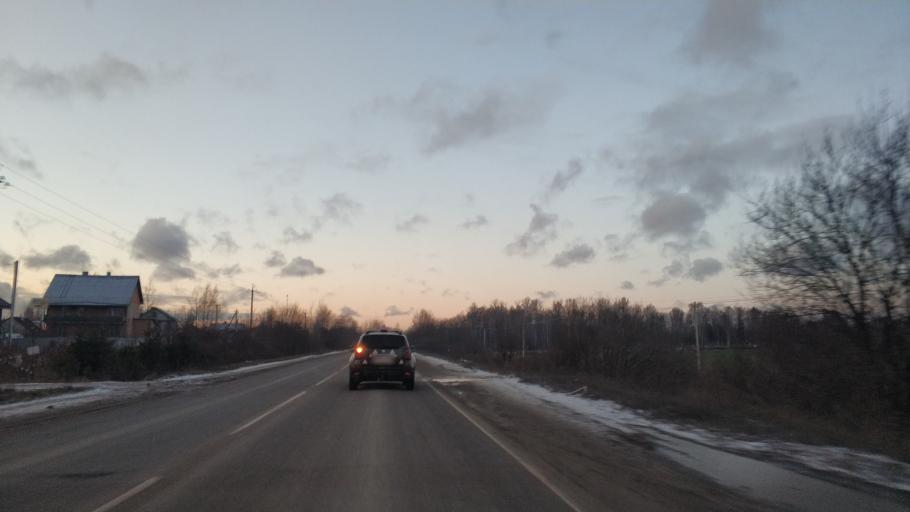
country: RU
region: St.-Petersburg
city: Pontonnyy
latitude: 59.8045
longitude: 30.6267
